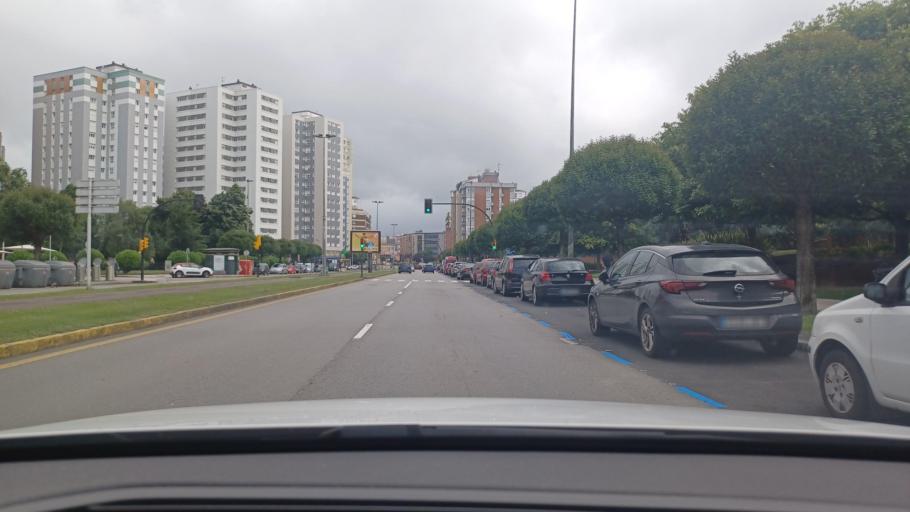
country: ES
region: Asturias
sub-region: Province of Asturias
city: Natahoyo
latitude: 43.5361
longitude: -5.6728
